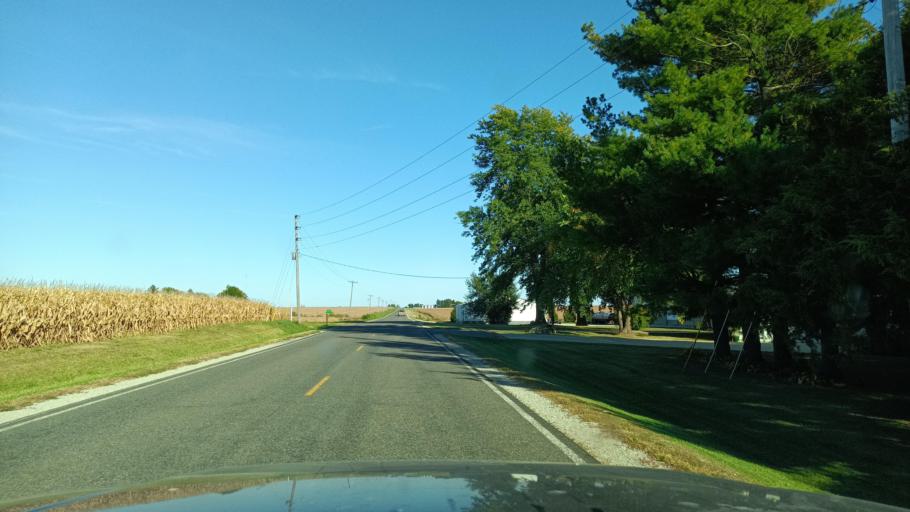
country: US
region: Illinois
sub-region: De Witt County
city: Clinton
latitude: 40.2244
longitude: -88.9053
